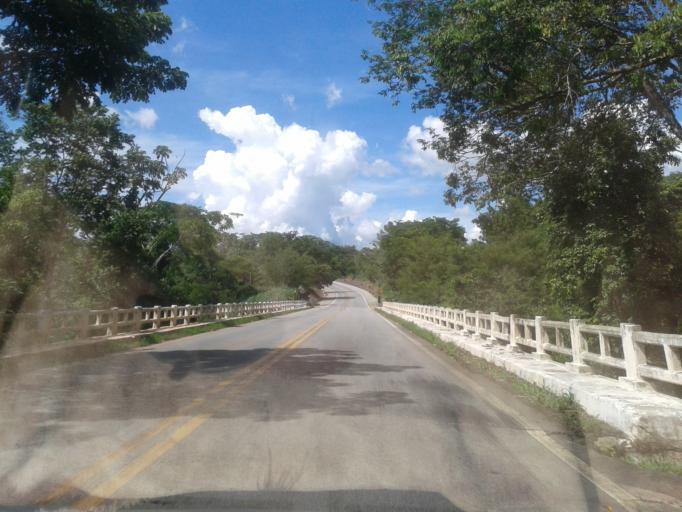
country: BR
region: Goias
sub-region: Goias
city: Goias
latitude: -15.7872
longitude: -50.1316
